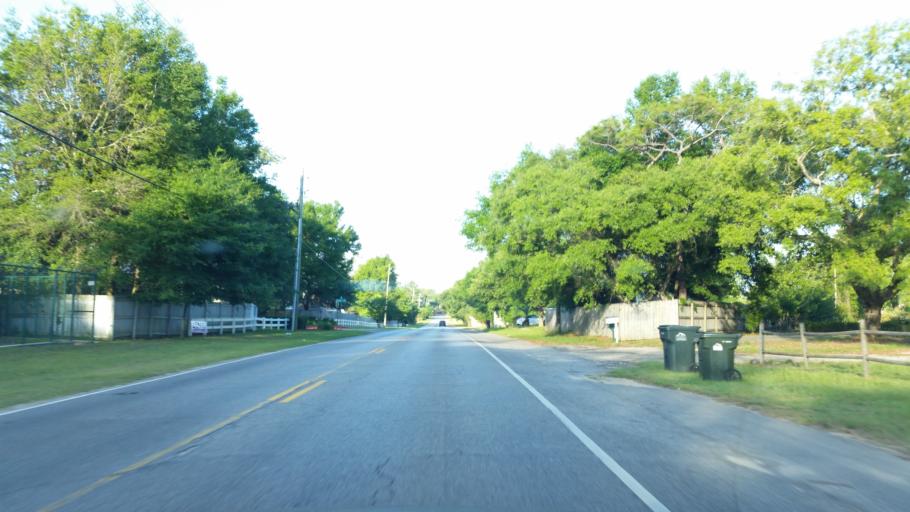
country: US
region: Florida
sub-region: Escambia County
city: Bellview
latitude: 30.4416
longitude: -87.3189
